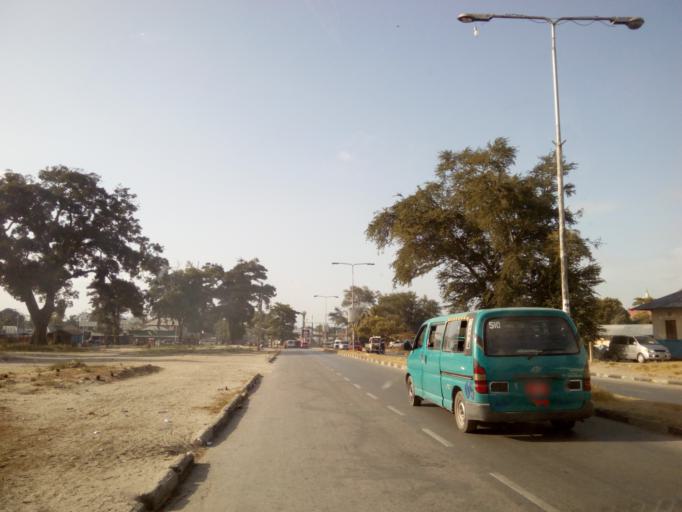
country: TZ
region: Zanzibar Urban/West
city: Zanzibar
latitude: -6.1640
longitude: 39.2040
